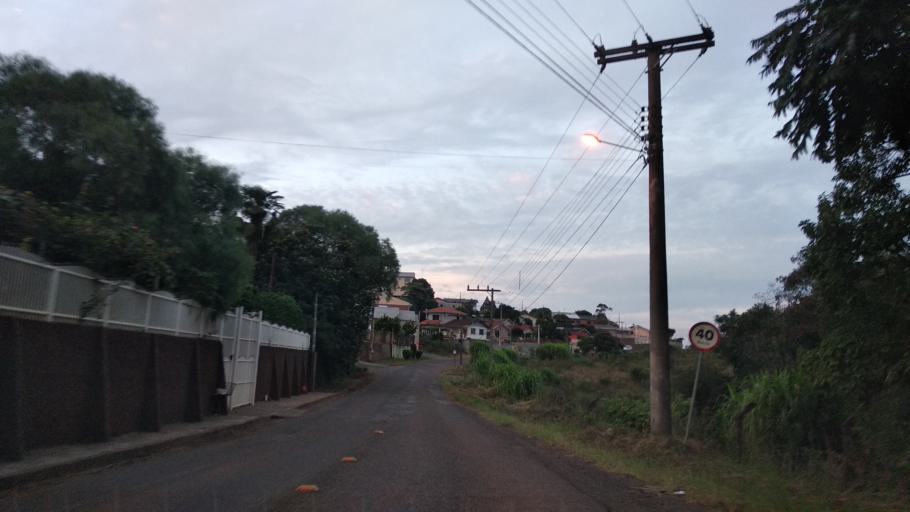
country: BR
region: Santa Catarina
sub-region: Videira
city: Videira
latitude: -26.9966
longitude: -51.1825
